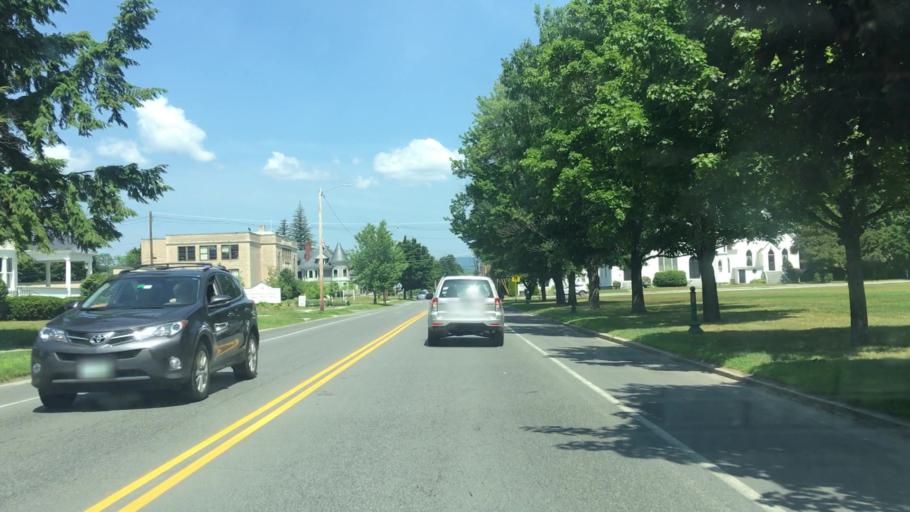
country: US
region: New Hampshire
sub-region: Sullivan County
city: Newport
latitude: 43.3664
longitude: -72.1749
